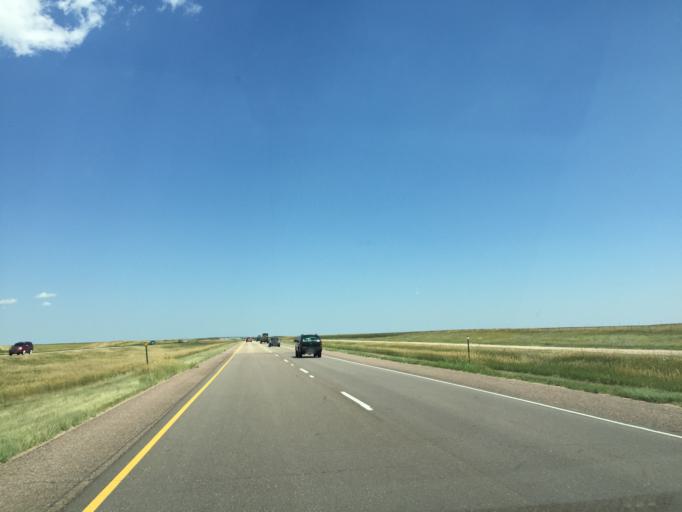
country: US
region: Colorado
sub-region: Lincoln County
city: Hugo
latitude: 39.2800
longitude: -103.3697
